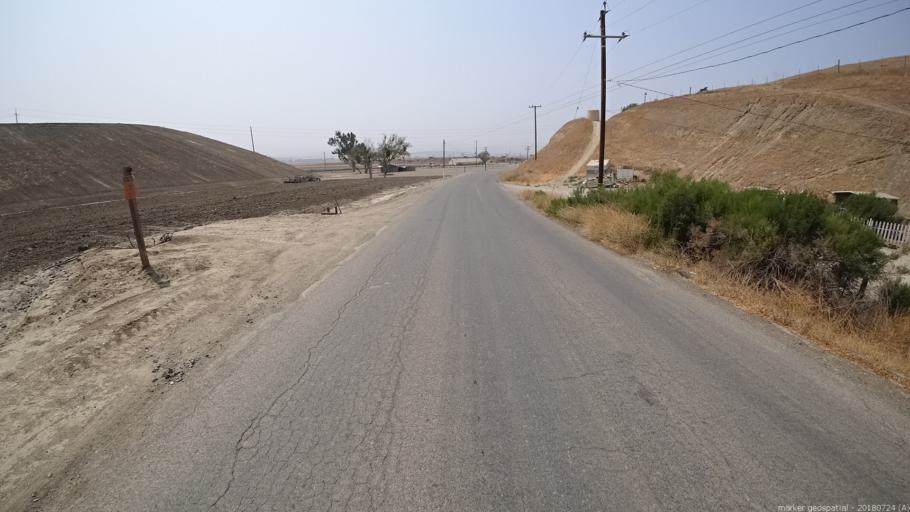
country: US
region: California
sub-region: Monterey County
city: King City
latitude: 36.1898
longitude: -121.0687
